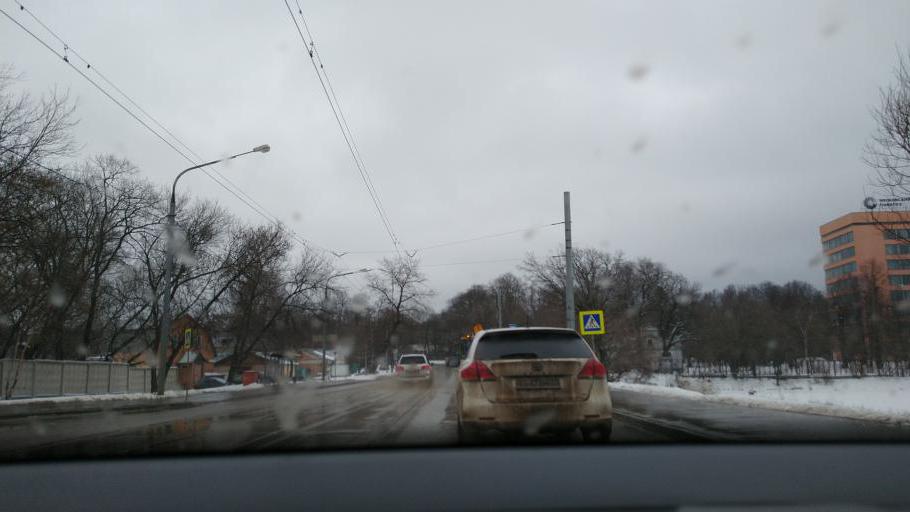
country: RU
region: Moscow
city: Likhobory
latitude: 55.8352
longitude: 37.5458
